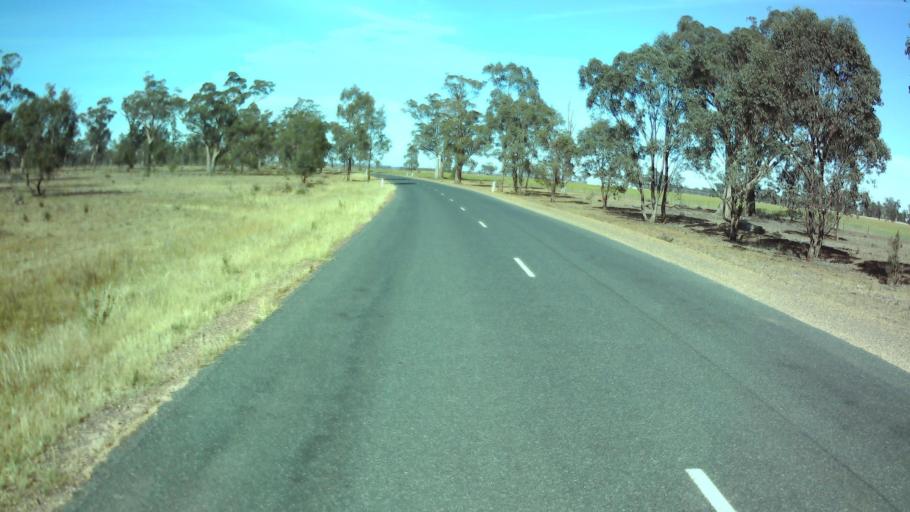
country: AU
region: New South Wales
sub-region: Weddin
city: Grenfell
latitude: -34.1145
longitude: 147.8224
